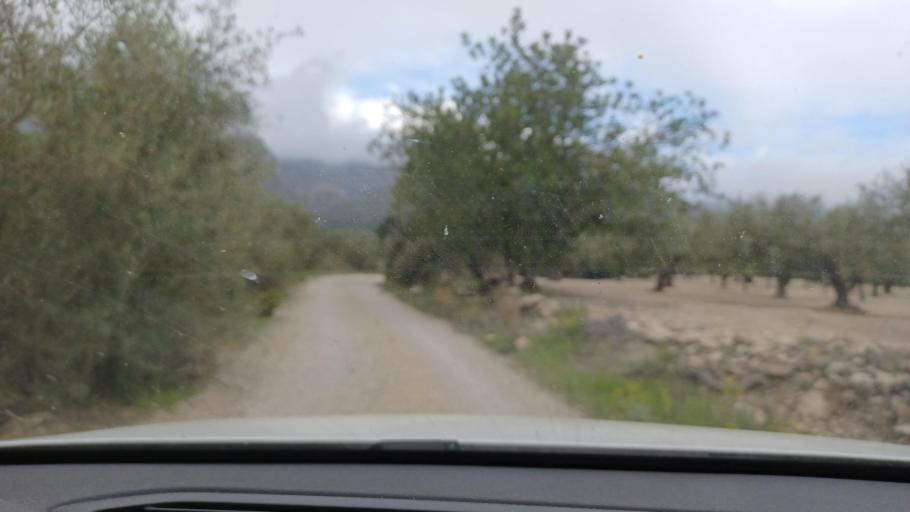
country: ES
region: Catalonia
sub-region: Provincia de Tarragona
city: Mas de Barberans
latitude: 40.8015
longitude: 0.4147
